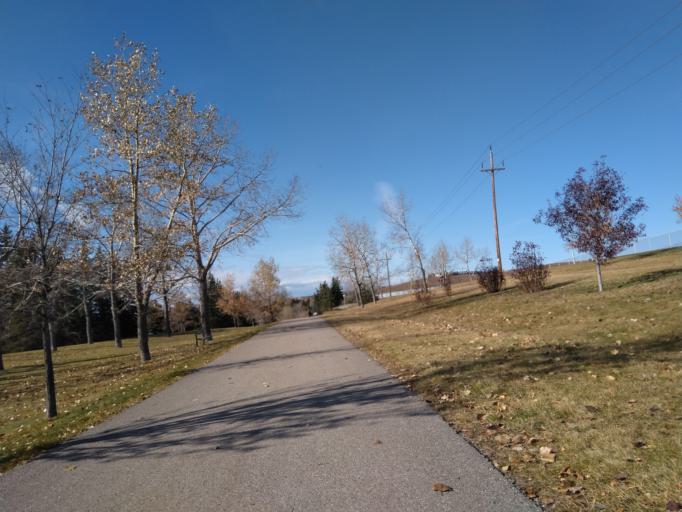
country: CA
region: Alberta
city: Calgary
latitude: 51.1002
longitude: -114.1230
